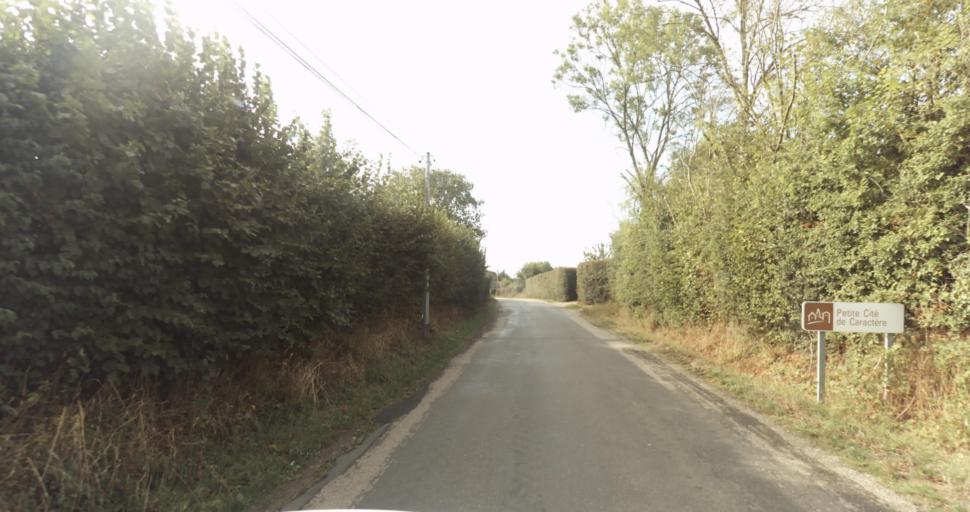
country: FR
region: Lower Normandy
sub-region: Departement de l'Orne
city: Gace
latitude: 48.8993
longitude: 0.3380
